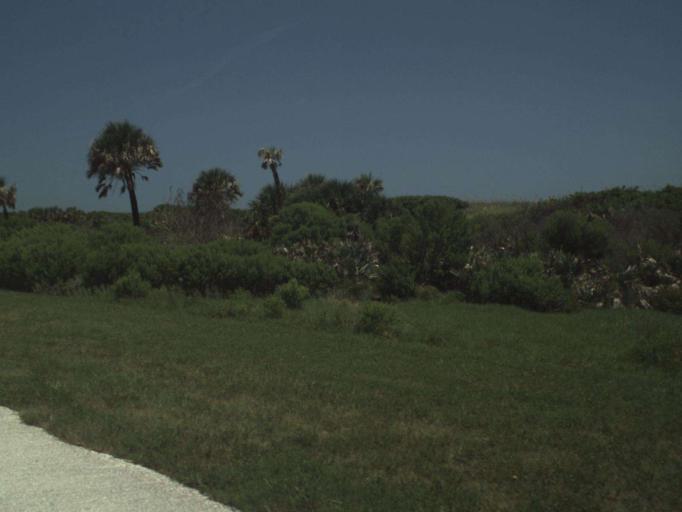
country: US
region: Florida
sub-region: Indian River County
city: Sebastian
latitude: 27.8428
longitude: -80.4395
